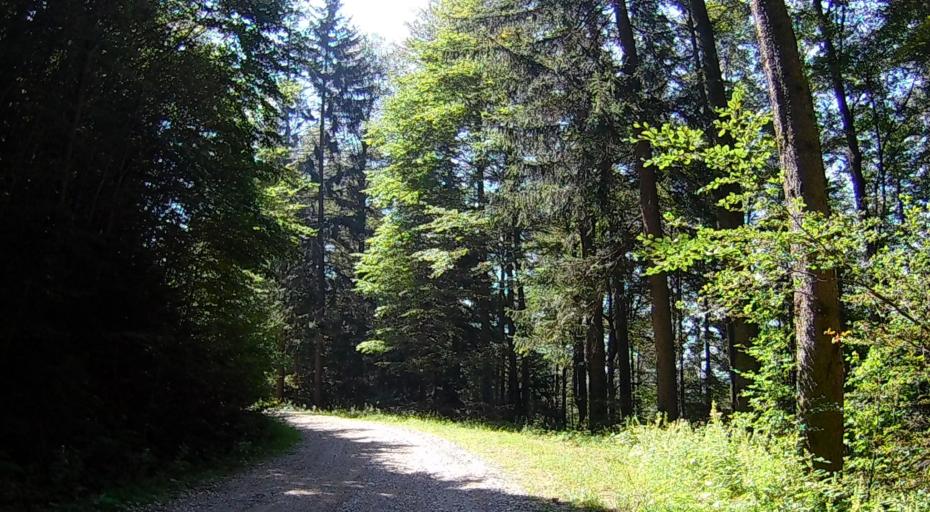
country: SI
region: Selnica ob Dravi
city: Selnica ob Dravi
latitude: 46.4969
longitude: 15.4630
